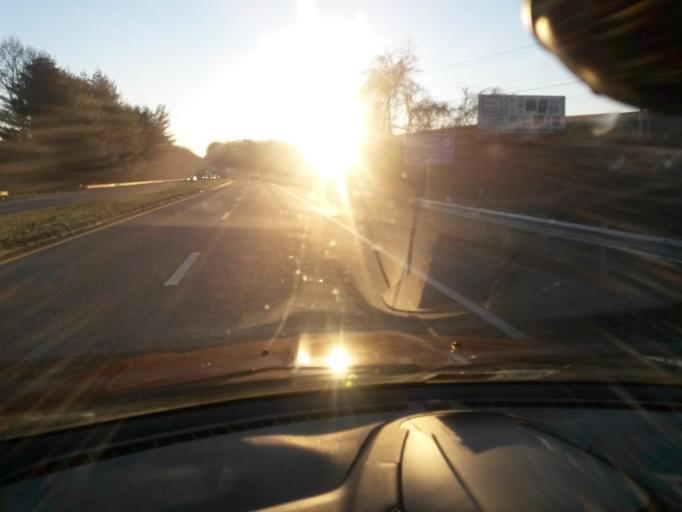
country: US
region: Virginia
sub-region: Franklin County
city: Rocky Mount
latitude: 37.0750
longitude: -79.9111
